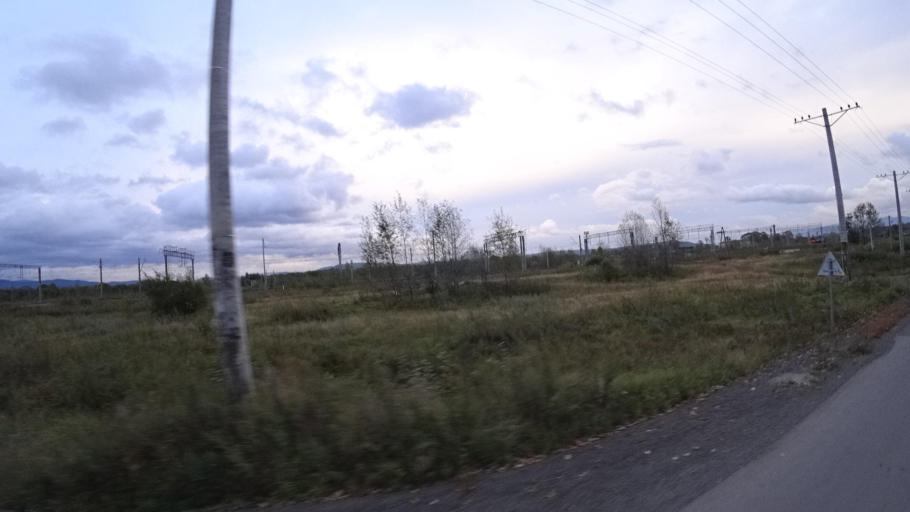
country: RU
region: Jewish Autonomous Oblast
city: Izvestkovyy
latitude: 48.9883
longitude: 131.5435
